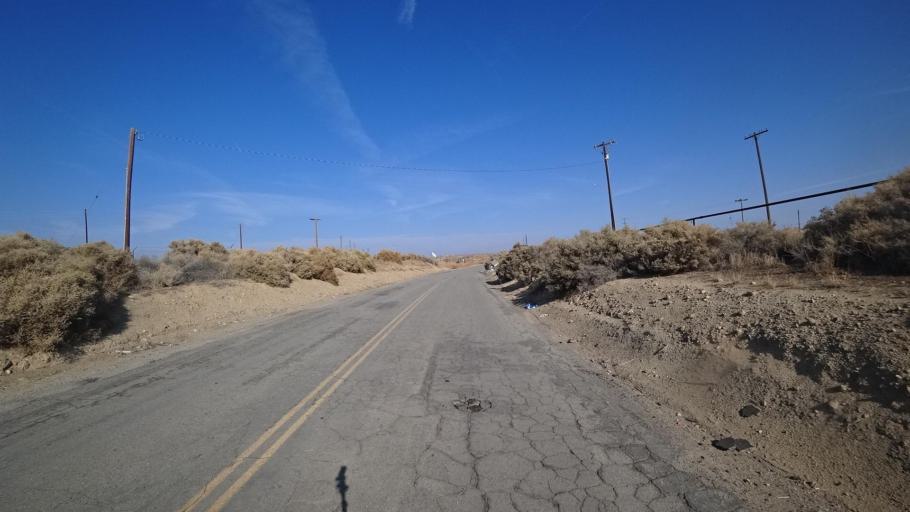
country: US
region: California
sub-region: Kern County
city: Oildale
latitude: 35.4613
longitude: -119.0491
